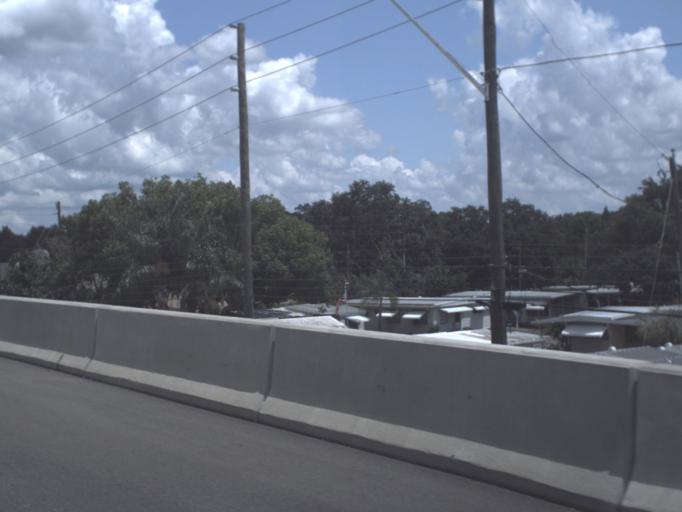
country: US
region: Florida
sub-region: Pinellas County
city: South Highpoint
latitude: 27.9524
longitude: -82.7300
